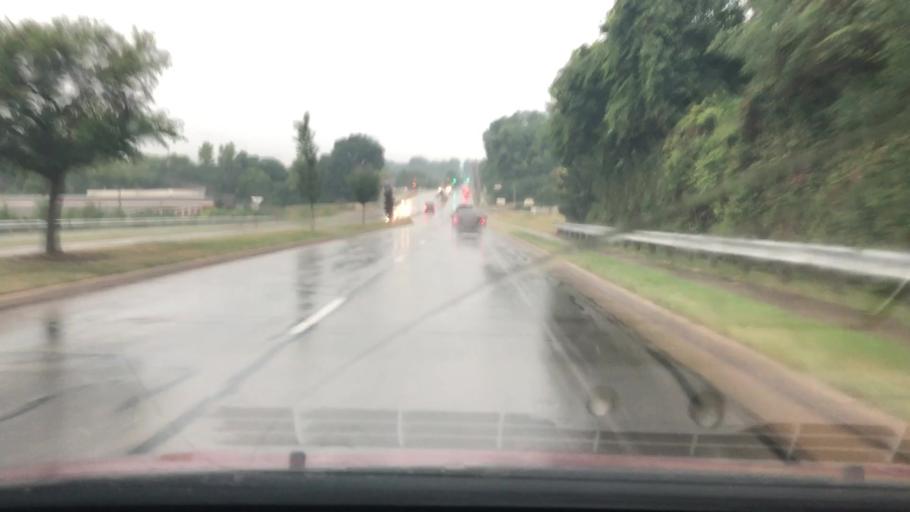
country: US
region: Ohio
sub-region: Montgomery County
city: Centerville
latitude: 39.6524
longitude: -84.1276
